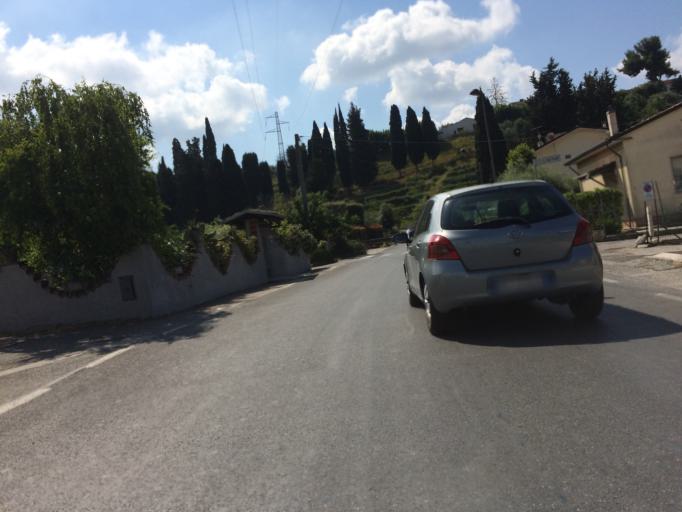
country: IT
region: Tuscany
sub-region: Provincia di Lucca
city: Massarosa
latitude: 43.8666
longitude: 10.3418
